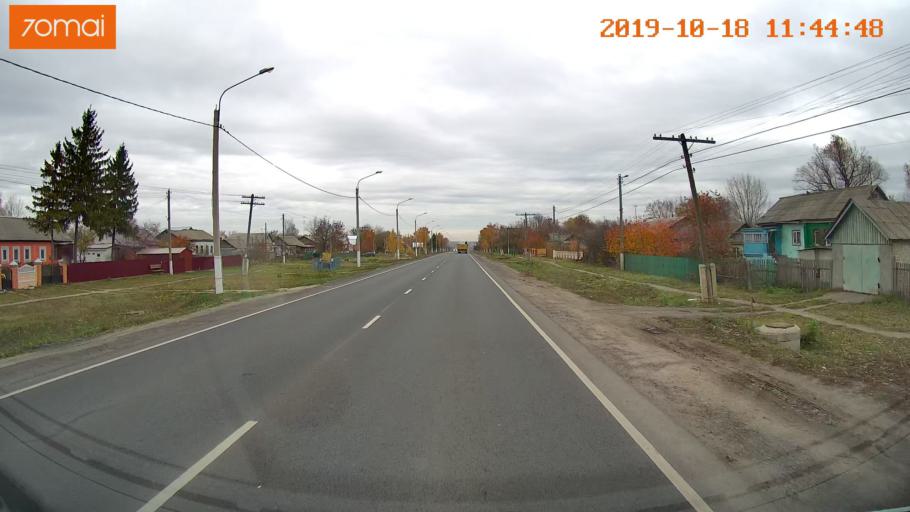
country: RU
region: Rjazan
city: Mikhaylov
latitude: 54.2051
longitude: 38.9622
